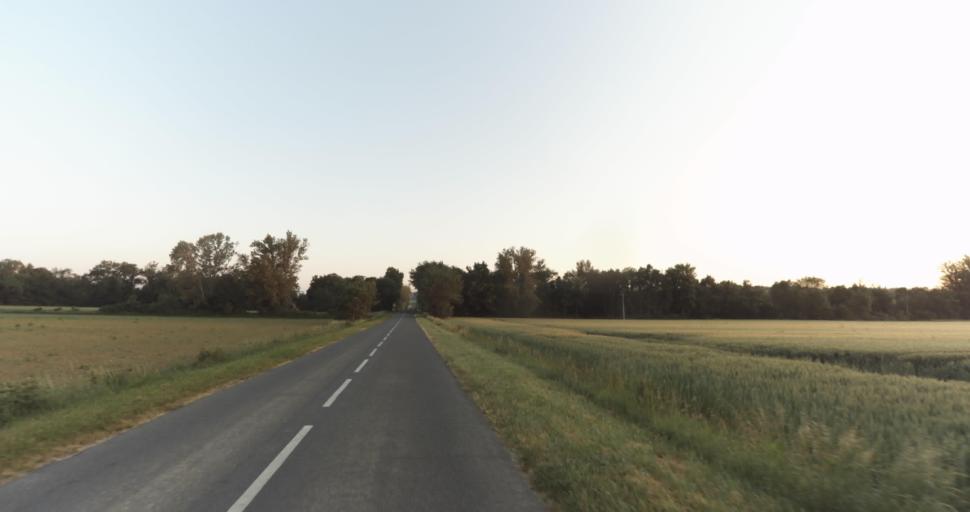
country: FR
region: Midi-Pyrenees
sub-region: Departement du Gers
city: Pujaudran
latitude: 43.6464
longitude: 1.1383
